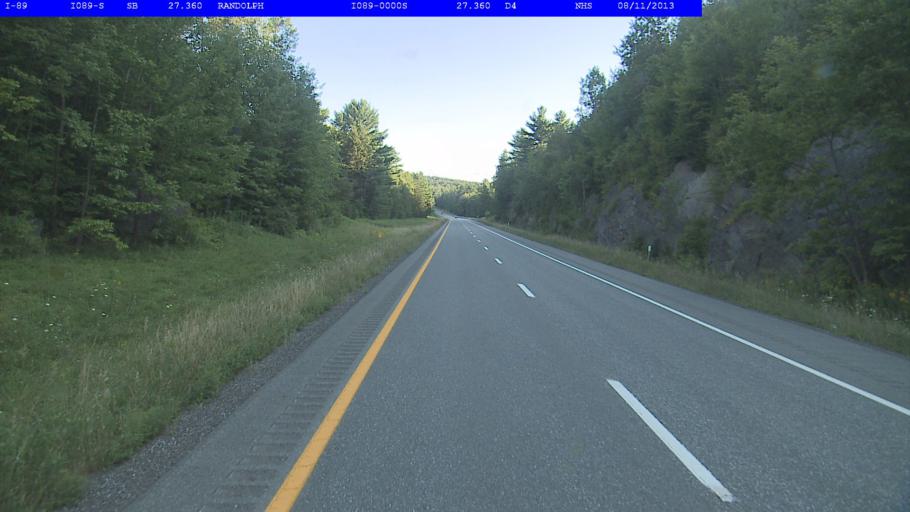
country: US
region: Vermont
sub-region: Orange County
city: Randolph
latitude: 43.8948
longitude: -72.6168
